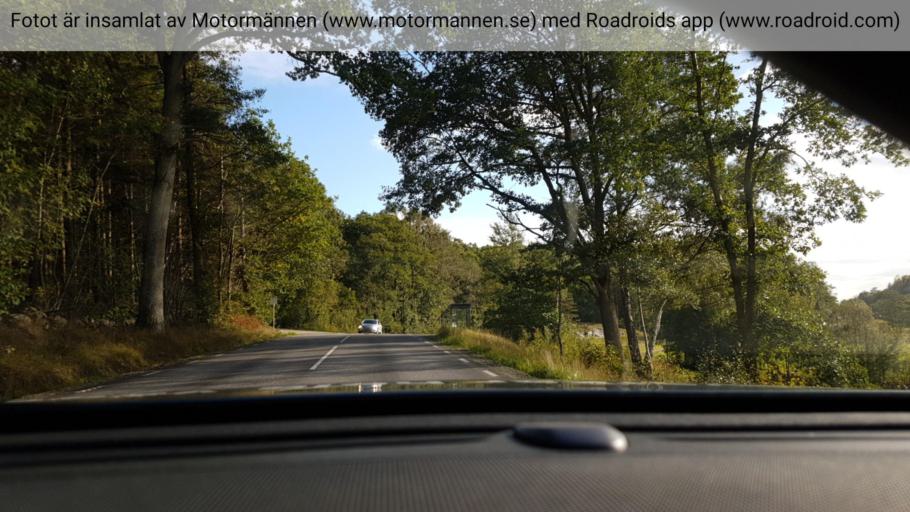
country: SE
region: Vaestra Goetaland
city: Svanesund
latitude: 58.1163
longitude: 11.8545
